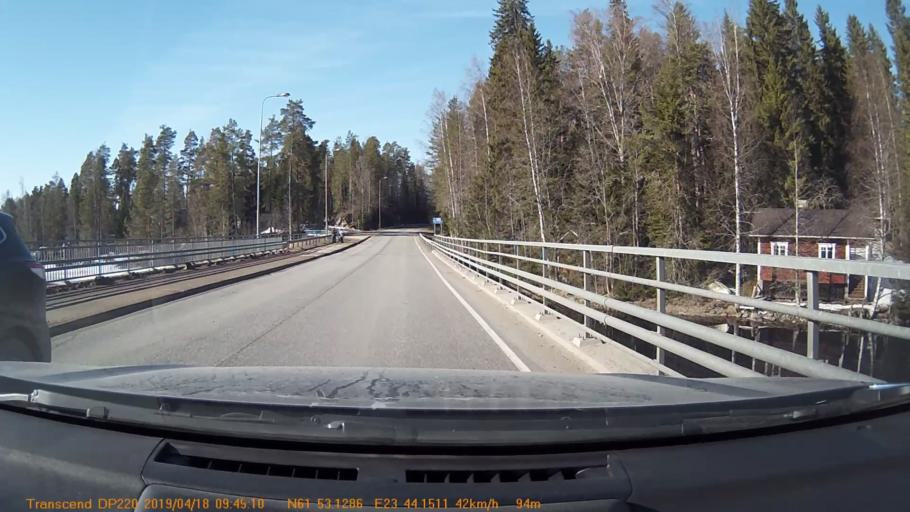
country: FI
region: Pirkanmaa
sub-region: Tampere
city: Kuru
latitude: 61.8855
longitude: 23.7359
